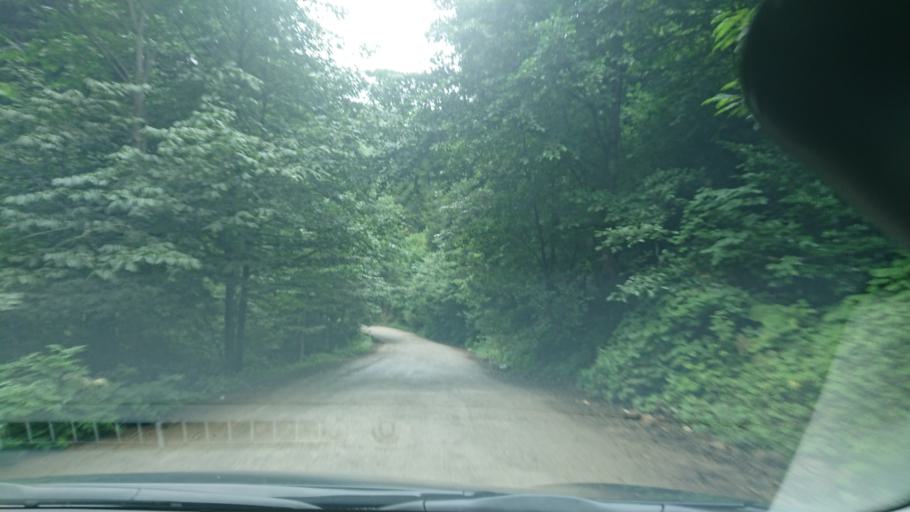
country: TR
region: Gumushane
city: Kurtun
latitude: 40.6668
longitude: 39.0396
